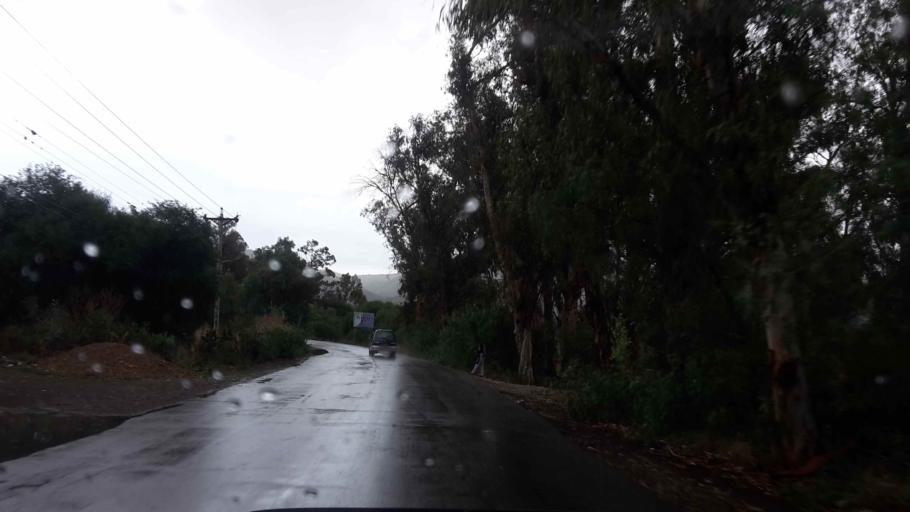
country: BO
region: Cochabamba
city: Tarata
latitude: -17.5415
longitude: -66.1071
